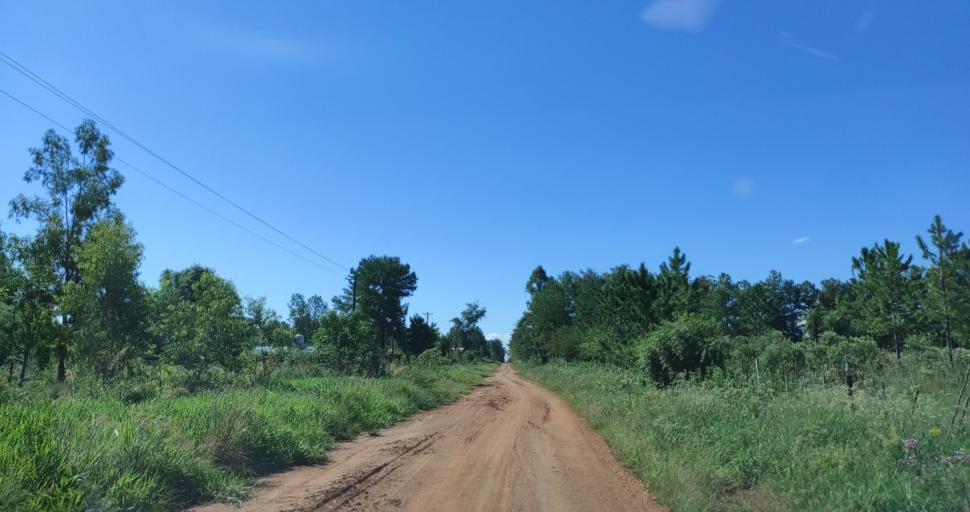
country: AR
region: Misiones
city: Garupa
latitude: -27.4719
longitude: -55.7983
